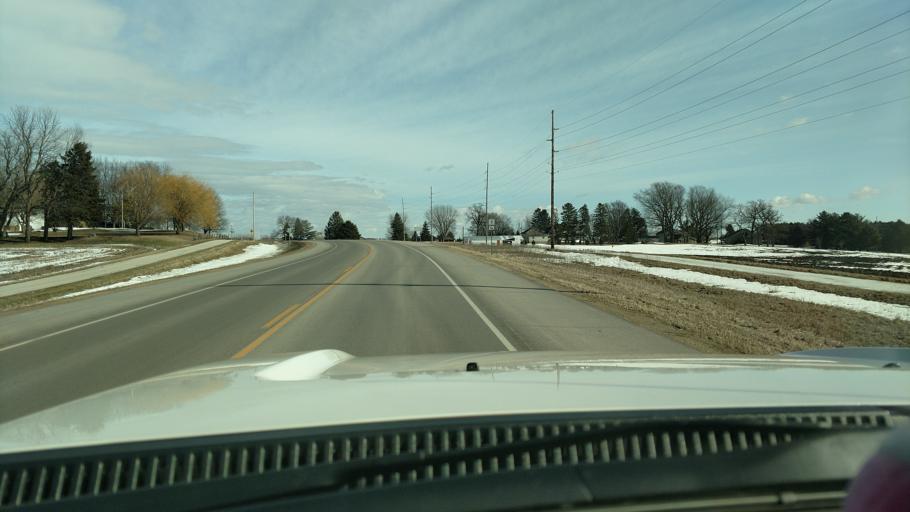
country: US
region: Minnesota
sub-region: Wabasha County
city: Plainview
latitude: 44.1578
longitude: -92.1734
